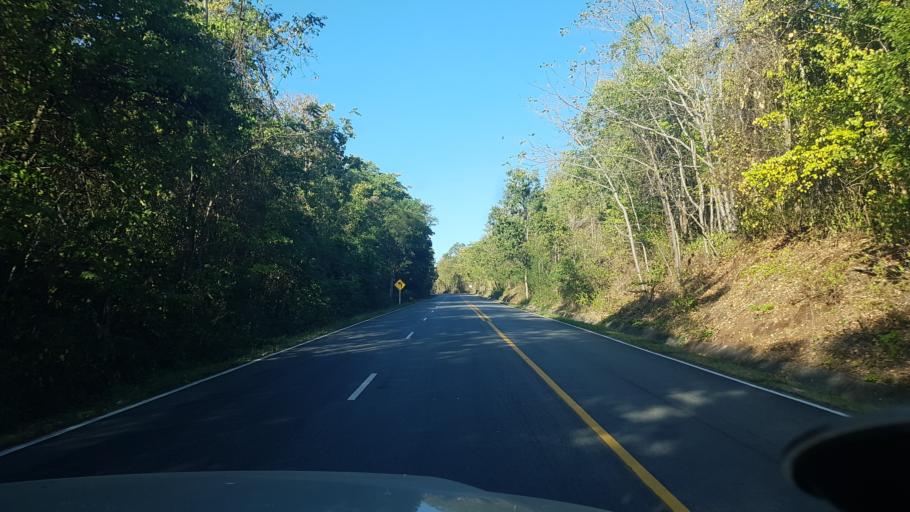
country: TH
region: Phetchabun
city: Nam Nao
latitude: 16.7031
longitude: 101.6535
